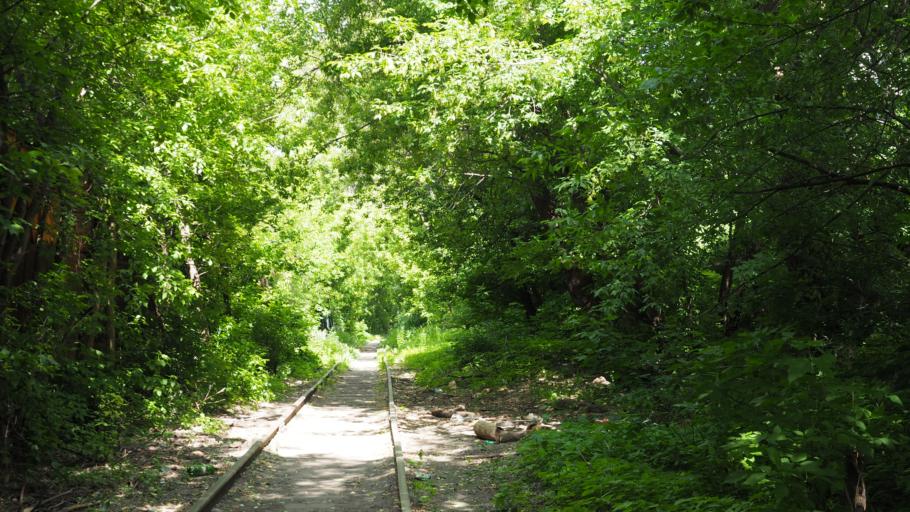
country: RU
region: Moskovskaya
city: Bogorodskoye
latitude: 55.7931
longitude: 37.7333
